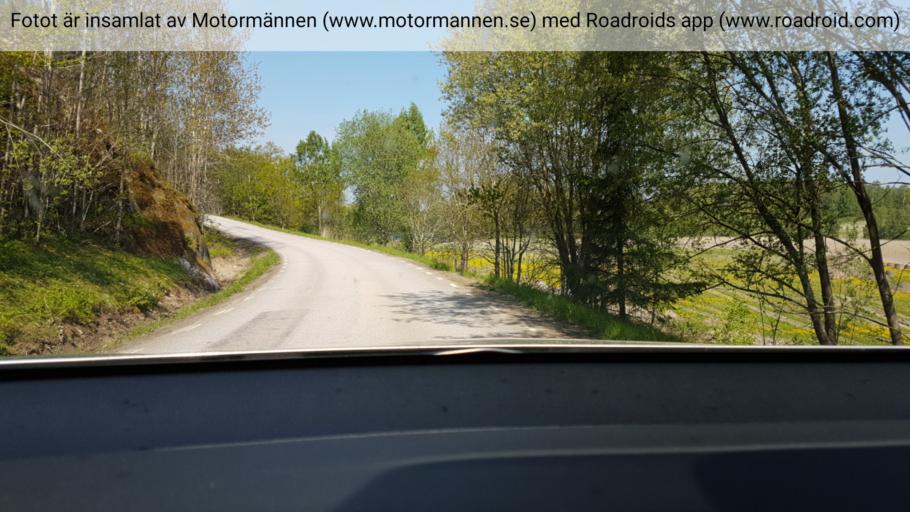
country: SE
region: Kalmar
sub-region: Vasterviks Kommun
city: Vaestervik
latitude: 57.8291
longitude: 16.5525
